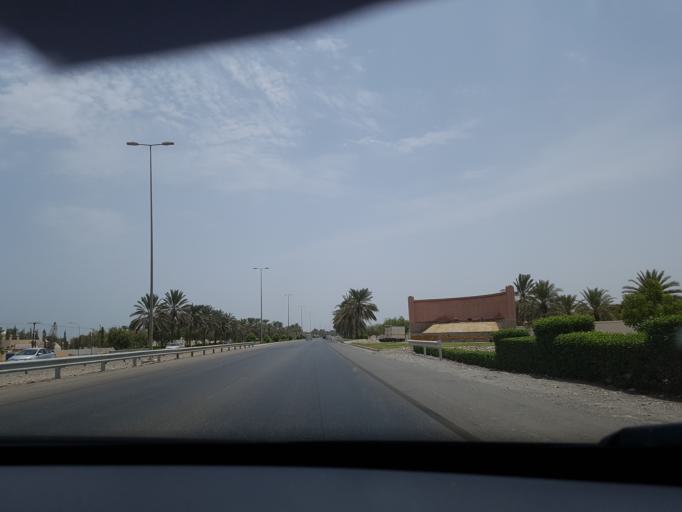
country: OM
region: Muhafazat Masqat
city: As Sib al Jadidah
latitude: 23.6933
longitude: 58.0627
